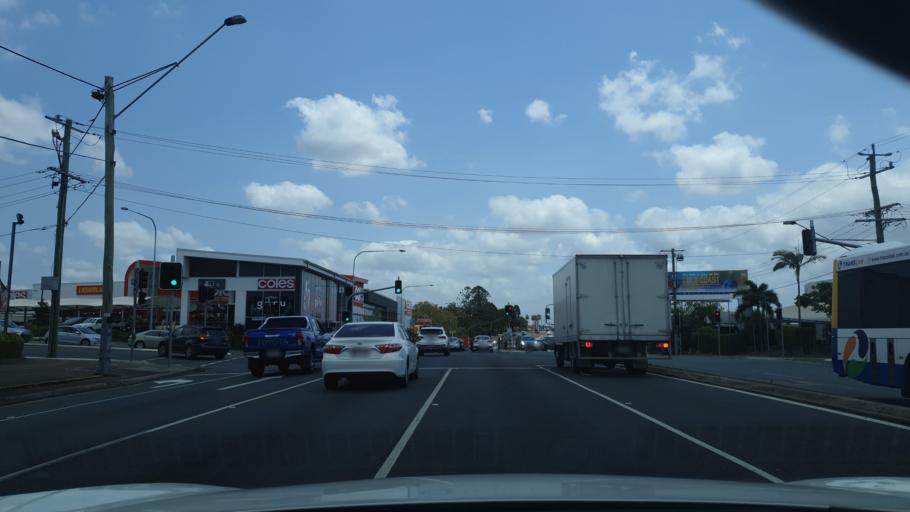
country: AU
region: Queensland
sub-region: Brisbane
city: Gordon Park
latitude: -27.4043
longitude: 153.0318
